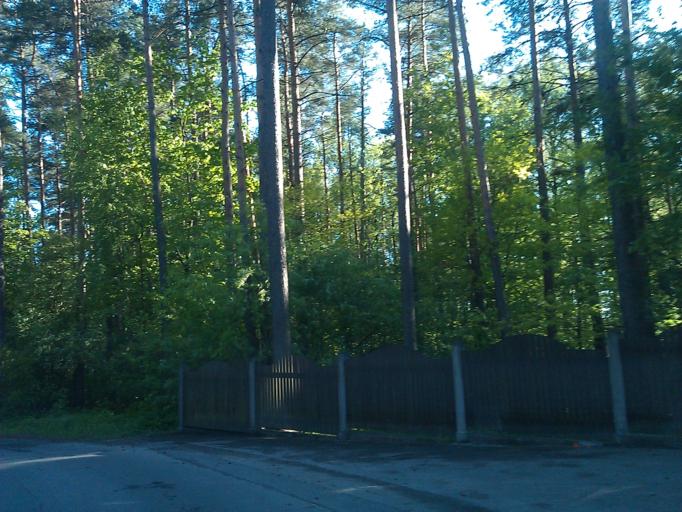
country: LV
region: Riga
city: Bergi
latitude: 57.0144
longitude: 24.2732
